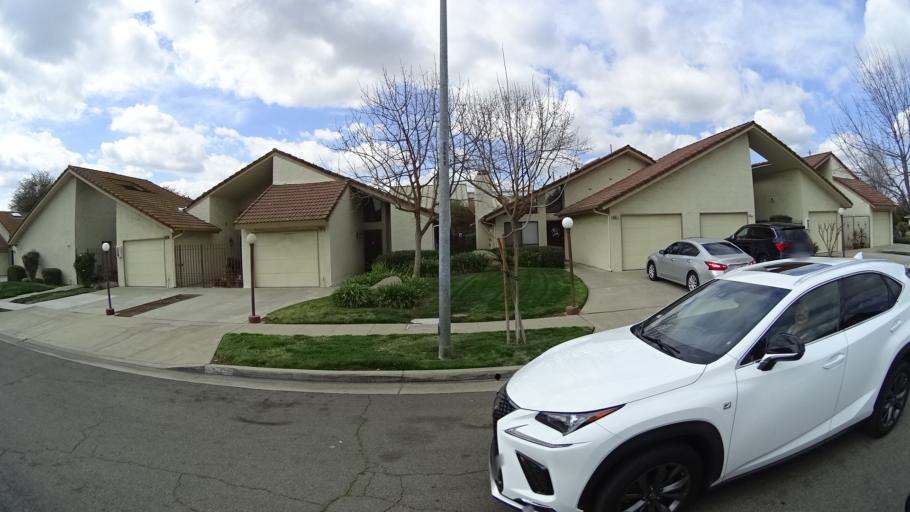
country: US
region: California
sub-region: Fresno County
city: Fresno
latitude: 36.8222
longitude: -119.8426
